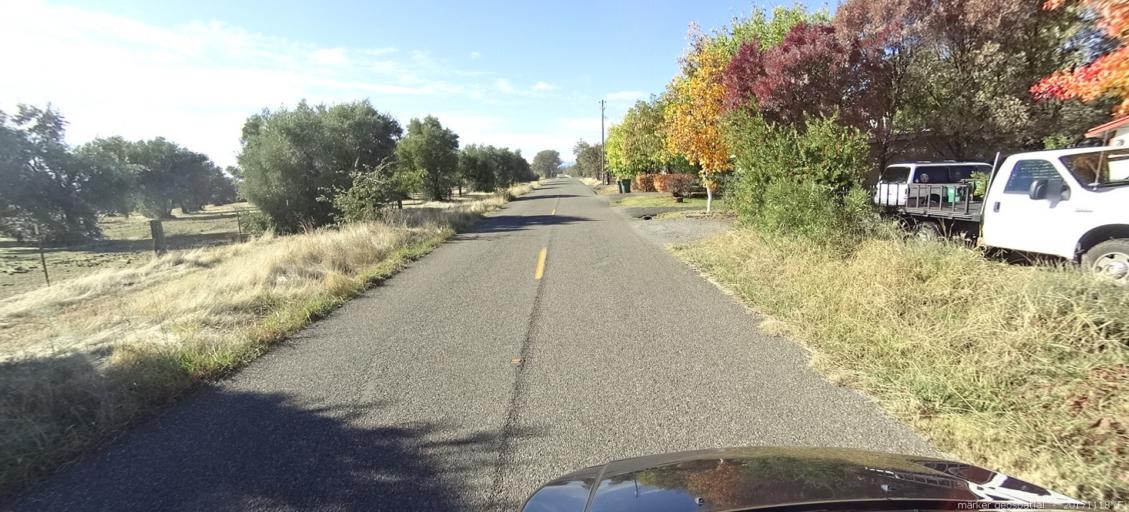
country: US
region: California
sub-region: Shasta County
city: Anderson
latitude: 40.4393
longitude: -122.4244
